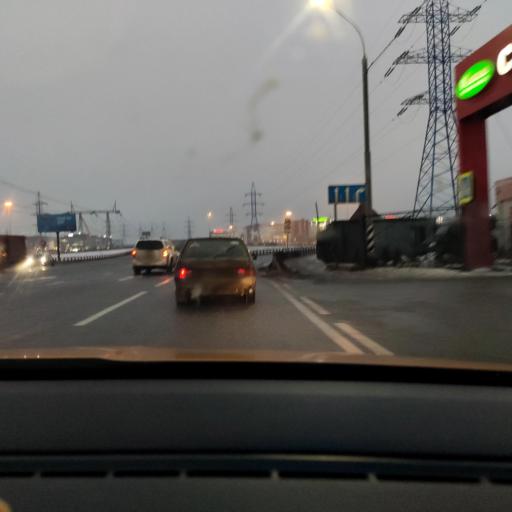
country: RU
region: Moskovskaya
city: Mosrentgen
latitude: 55.6273
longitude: 37.4398
